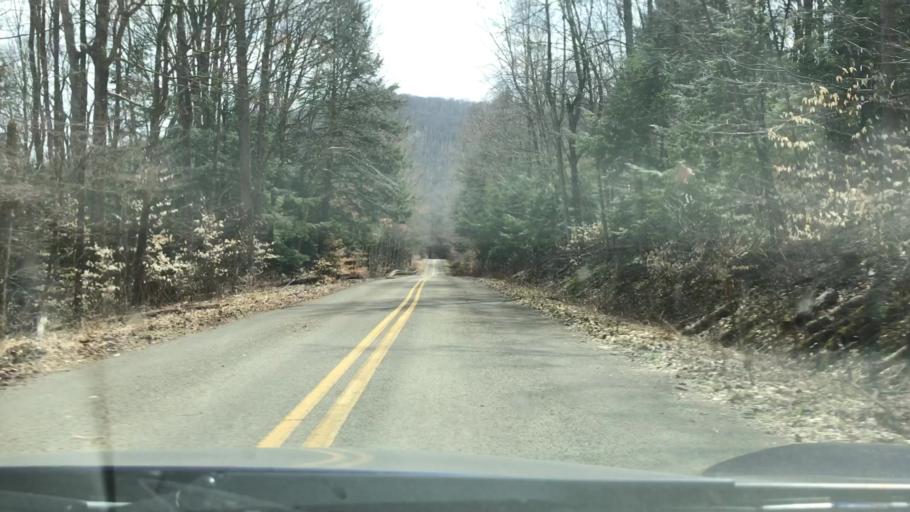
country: US
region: Pennsylvania
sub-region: Warren County
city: Sheffield
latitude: 41.8147
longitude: -78.9405
